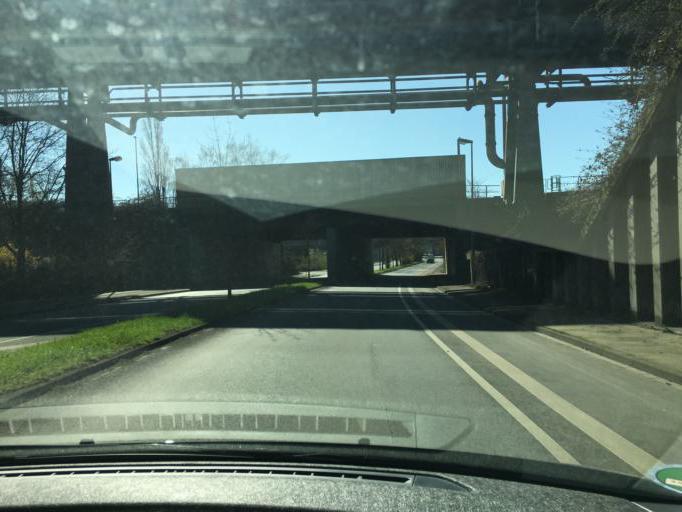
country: DE
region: North Rhine-Westphalia
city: Meiderich
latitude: 51.4831
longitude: 6.7275
